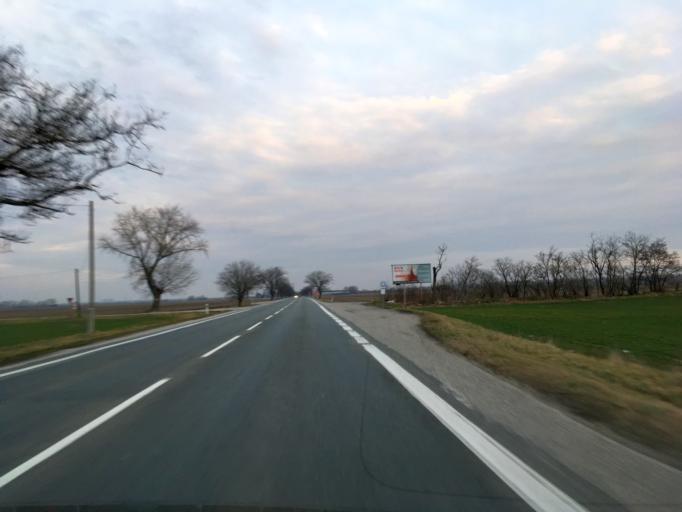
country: HU
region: Komarom-Esztergom
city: Acs
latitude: 47.7665
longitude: 17.9952
